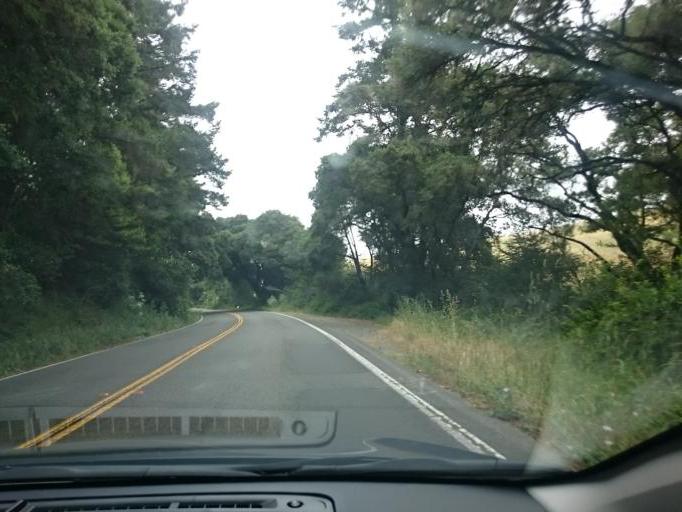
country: US
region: California
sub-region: Marin County
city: Lagunitas-Forest Knolls
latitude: 38.0190
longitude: -122.7715
